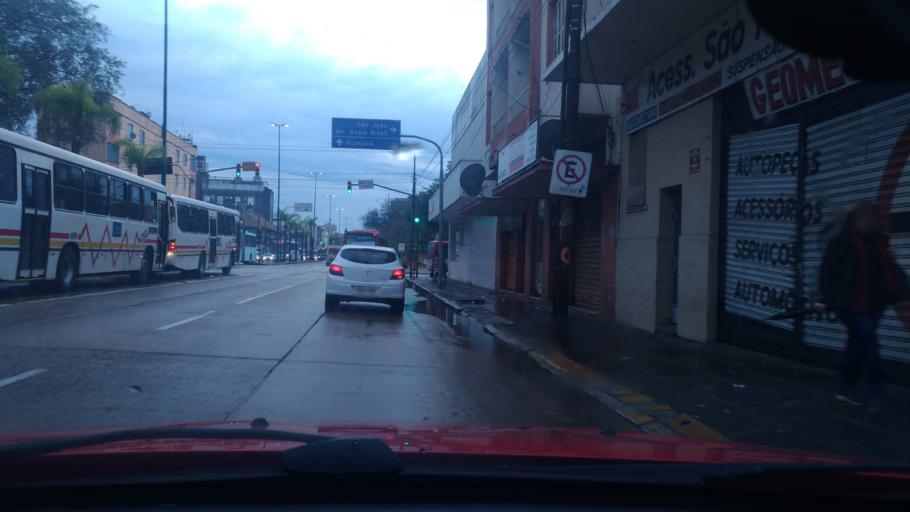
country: BR
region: Rio Grande do Sul
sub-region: Porto Alegre
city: Porto Alegre
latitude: -30.0058
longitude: -51.2008
